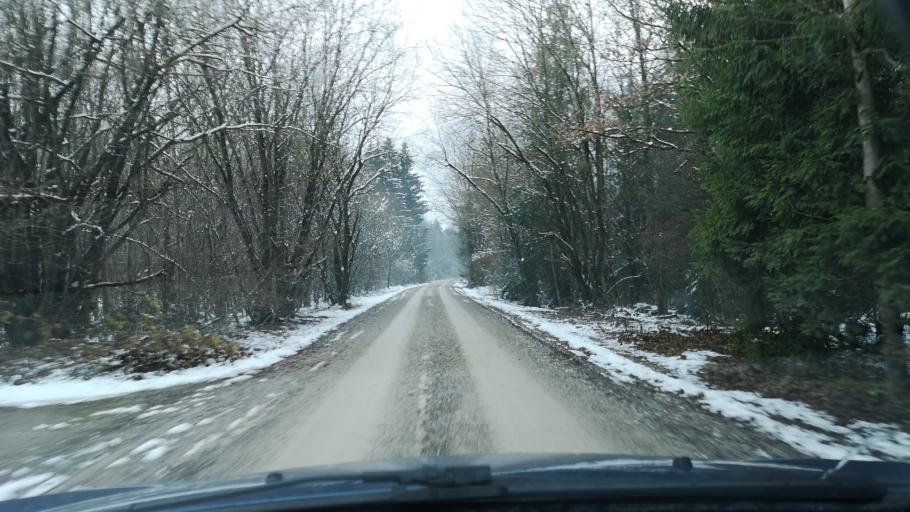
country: DE
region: Bavaria
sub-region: Upper Bavaria
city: Anzing
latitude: 48.1349
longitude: 11.8754
